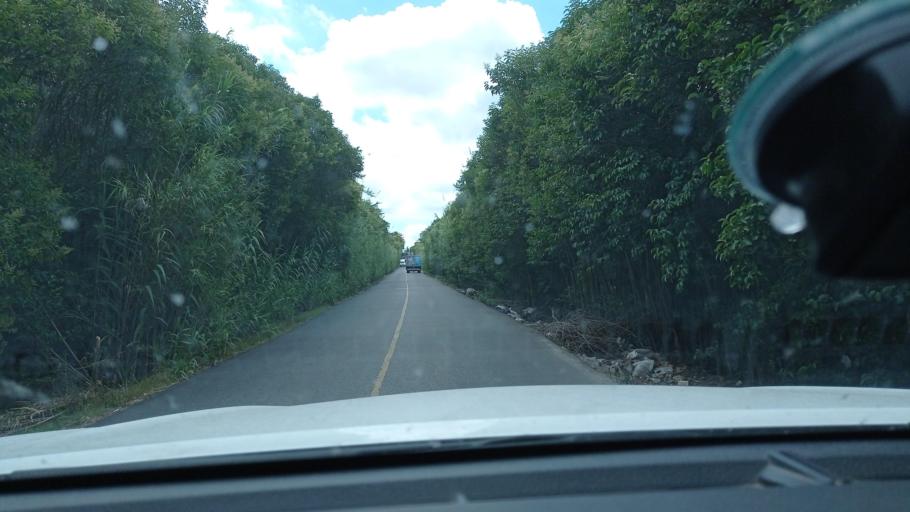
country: UY
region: Canelones
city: La Paz
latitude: -34.8074
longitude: -56.2014
